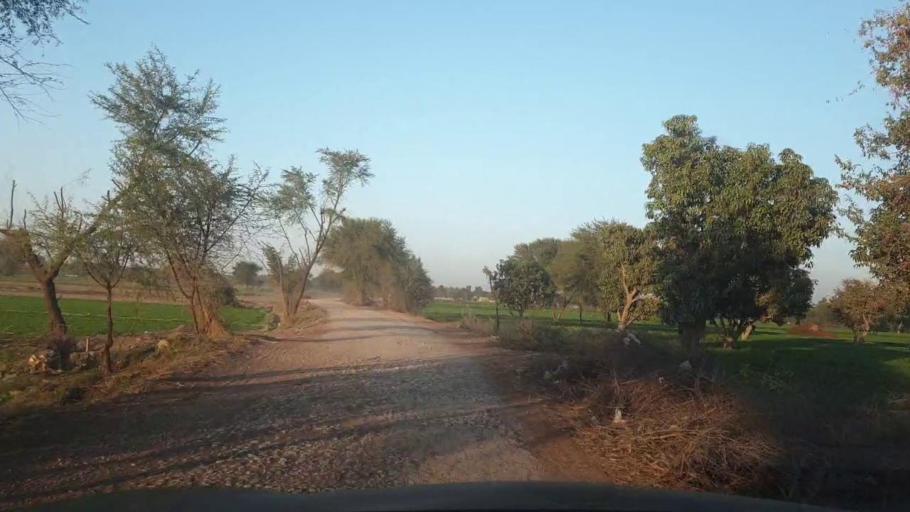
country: PK
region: Sindh
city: Ubauro
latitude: 28.1735
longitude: 69.6025
